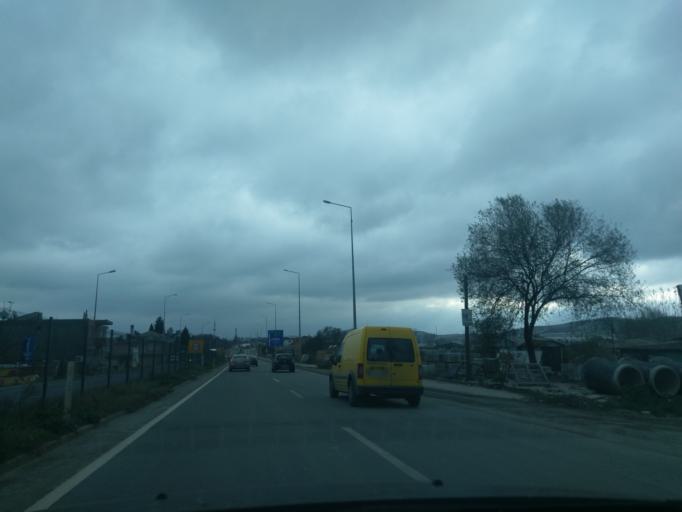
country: TR
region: Istanbul
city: Muratbey
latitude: 41.0933
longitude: 28.5127
